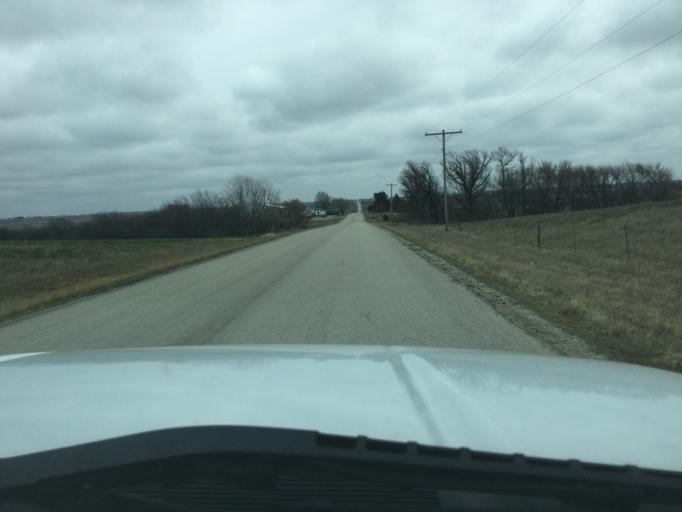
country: US
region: Kansas
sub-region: Nemaha County
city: Seneca
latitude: 39.7399
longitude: -96.0206
